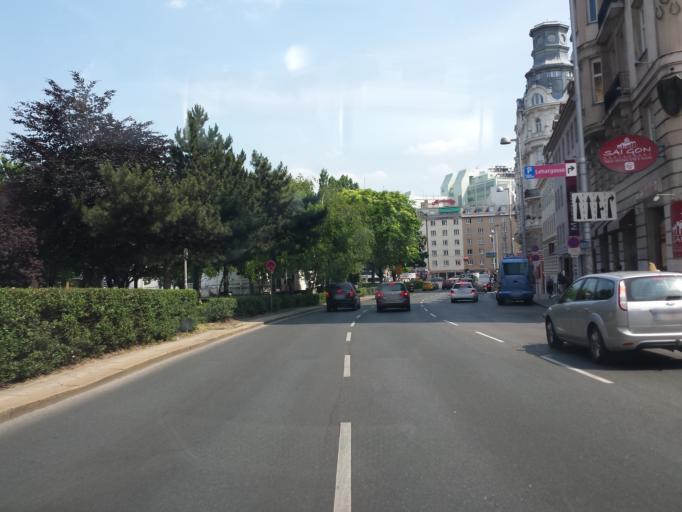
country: AT
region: Vienna
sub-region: Wien Stadt
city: Vienna
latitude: 48.2010
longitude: 16.3643
